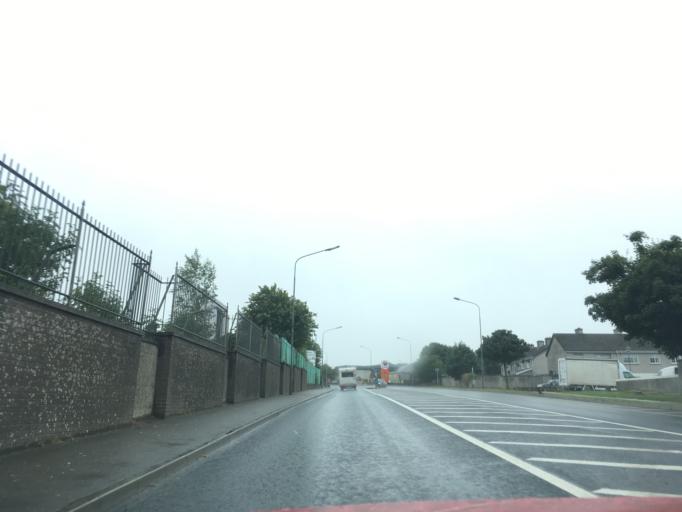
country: IE
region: Leinster
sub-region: Loch Garman
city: New Ross
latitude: 52.3939
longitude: -6.9340
